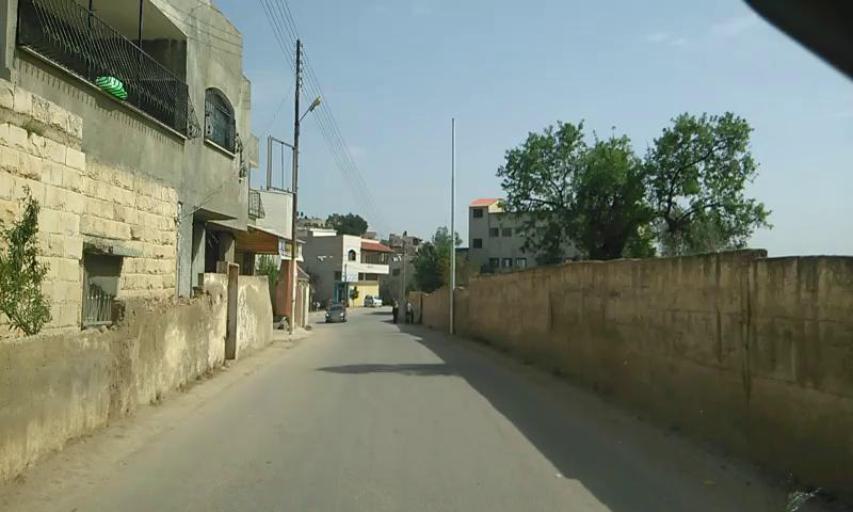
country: PS
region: West Bank
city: Birqin
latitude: 32.4514
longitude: 35.2627
